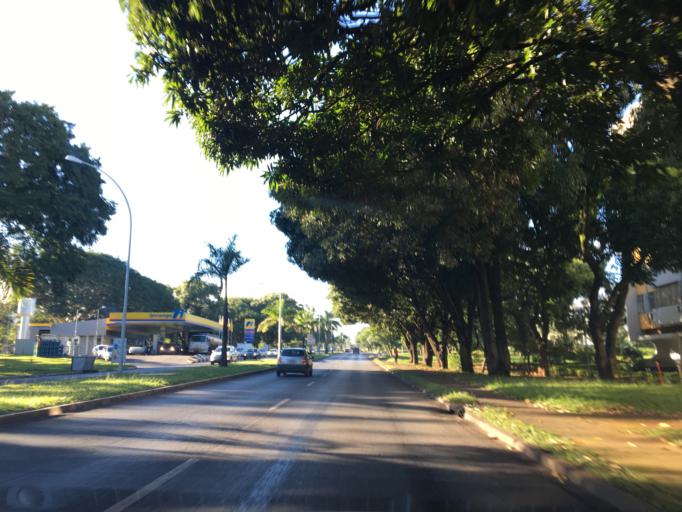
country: BR
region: Federal District
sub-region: Brasilia
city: Brasilia
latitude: -15.7537
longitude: -47.8876
